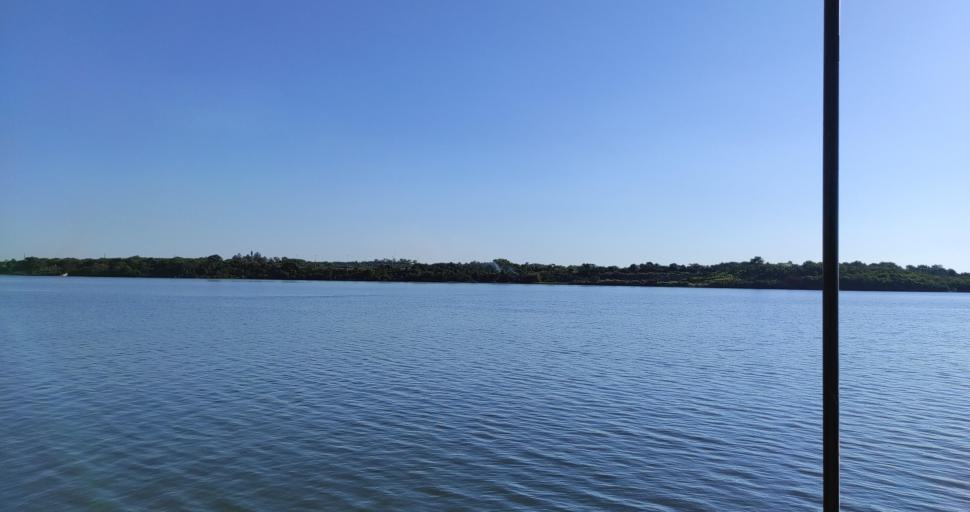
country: AR
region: Misiones
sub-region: Departamento de Capital
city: Posadas
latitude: -27.3646
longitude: -55.9577
